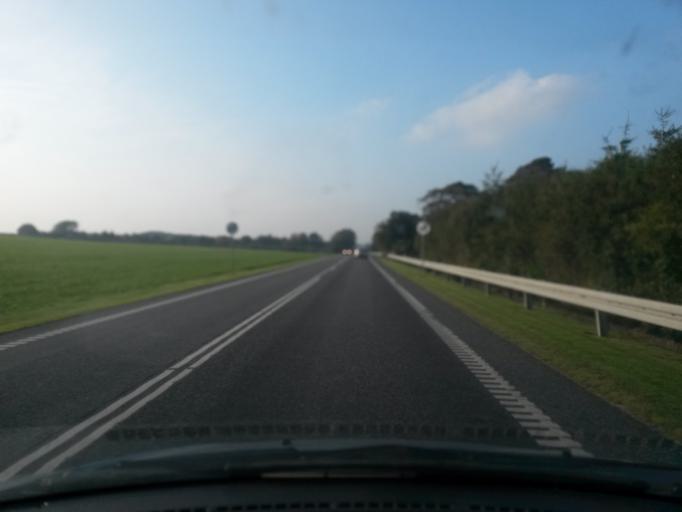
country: DK
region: Central Jutland
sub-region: Norddjurs Kommune
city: Allingabro
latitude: 56.3967
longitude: 10.2594
